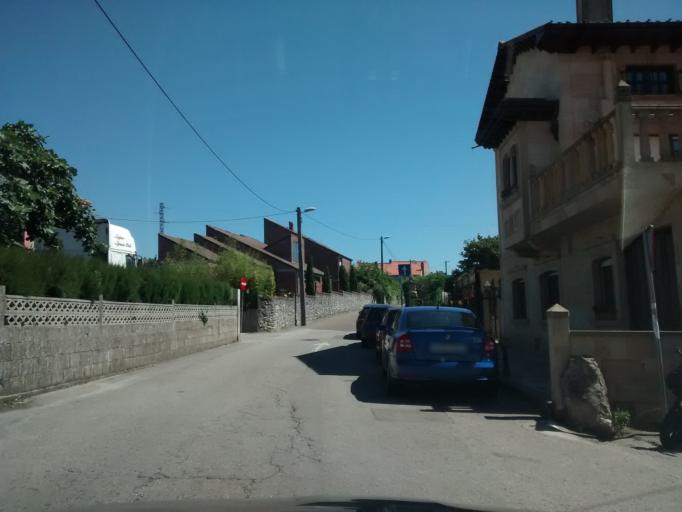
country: ES
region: Cantabria
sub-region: Provincia de Cantabria
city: Santander
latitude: 43.4708
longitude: -3.8305
